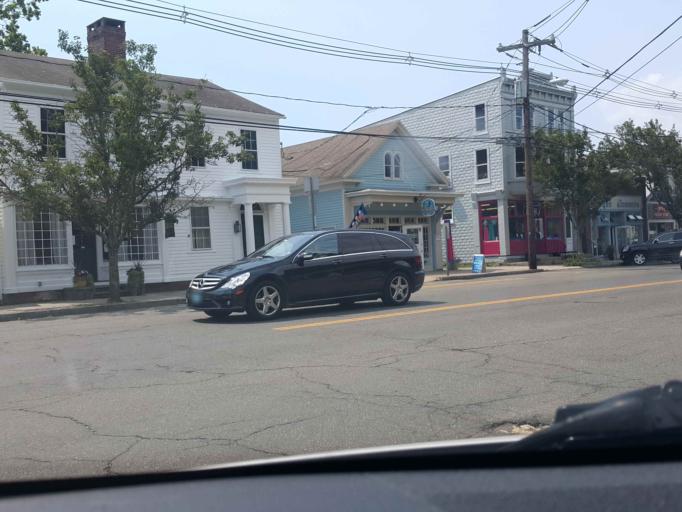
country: US
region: Connecticut
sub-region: New Haven County
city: Guilford Center
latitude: 41.2819
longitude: -72.6806
